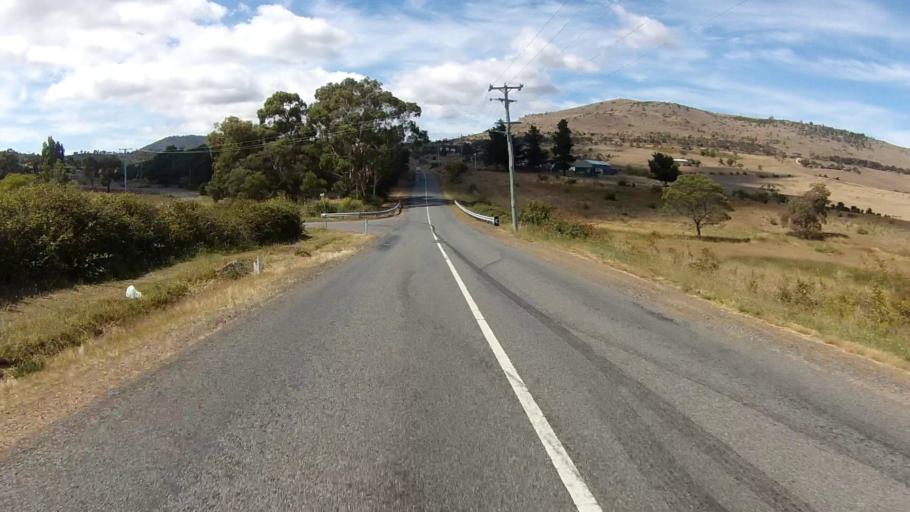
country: AU
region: Tasmania
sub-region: Brighton
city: Bridgewater
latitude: -42.7199
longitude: 147.2789
